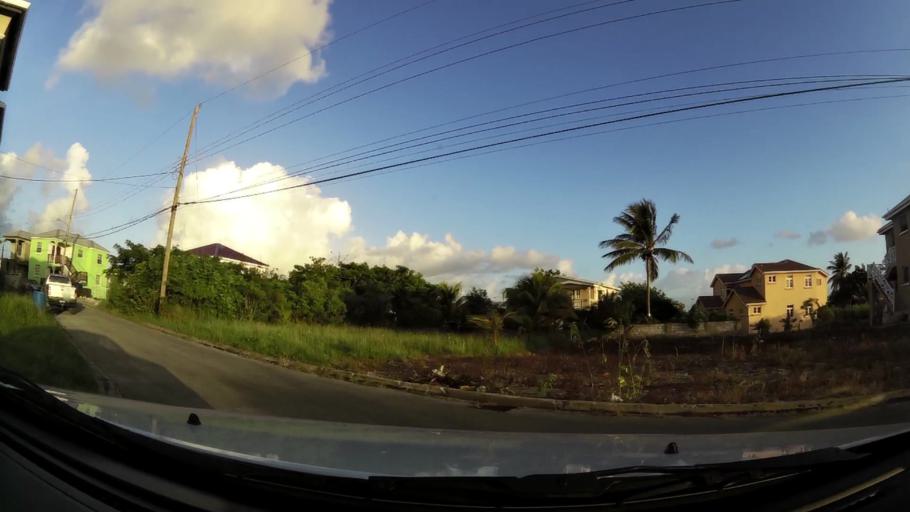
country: BB
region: Saint Philip
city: Crane
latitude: 13.1030
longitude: -59.4681
